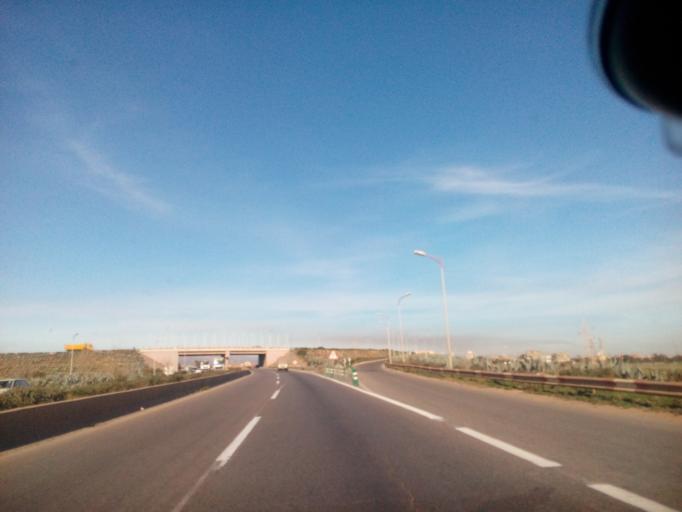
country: DZ
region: Oran
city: Ain el Bya
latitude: 35.7986
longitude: -0.2924
